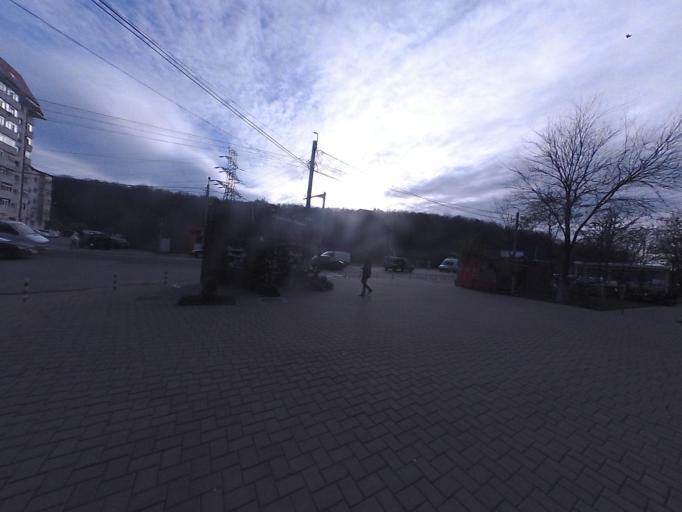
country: RO
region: Iasi
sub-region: Municipiul Iasi
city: Iasi
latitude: 47.1358
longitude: 27.5872
